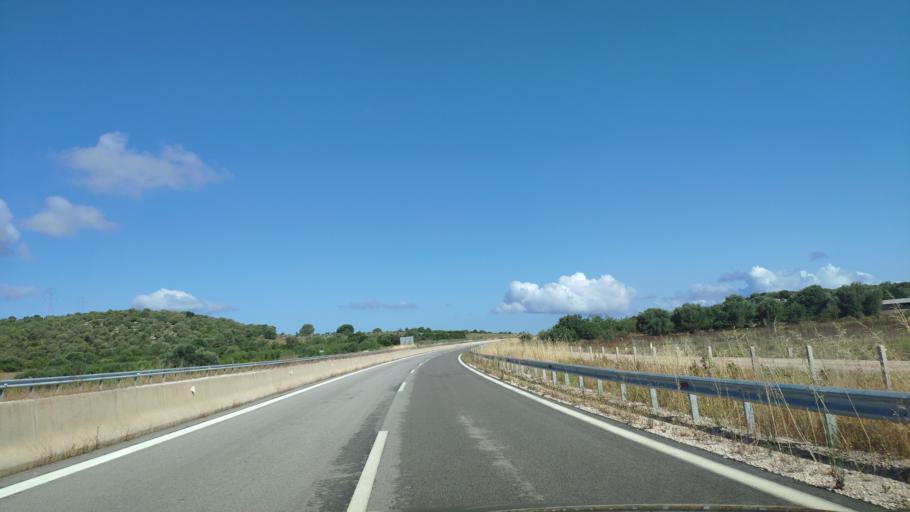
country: GR
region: West Greece
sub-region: Nomos Aitolias kai Akarnanias
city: Vonitsa
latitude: 38.9049
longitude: 20.8530
